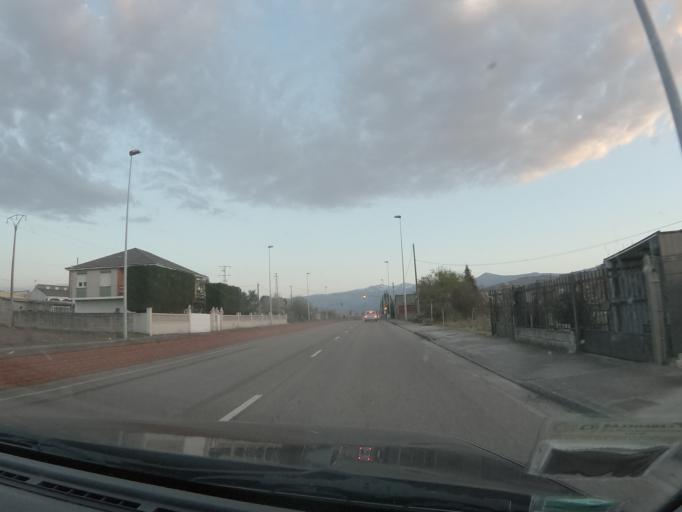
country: ES
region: Castille and Leon
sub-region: Provincia de Leon
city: Ponferrada
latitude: 42.5735
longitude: -6.6091
